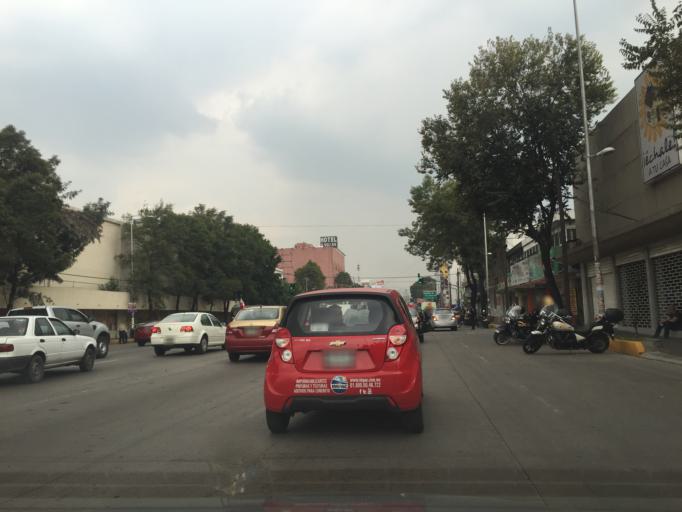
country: MX
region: Mexico City
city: Colonia del Valle
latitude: 19.3799
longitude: -99.1872
